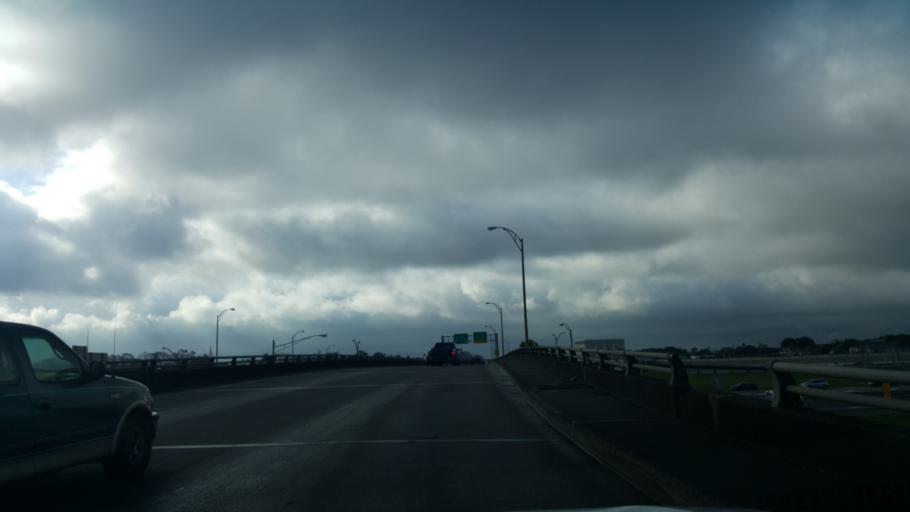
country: US
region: Louisiana
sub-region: Jefferson Parish
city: Metairie
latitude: 29.9966
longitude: -90.1160
